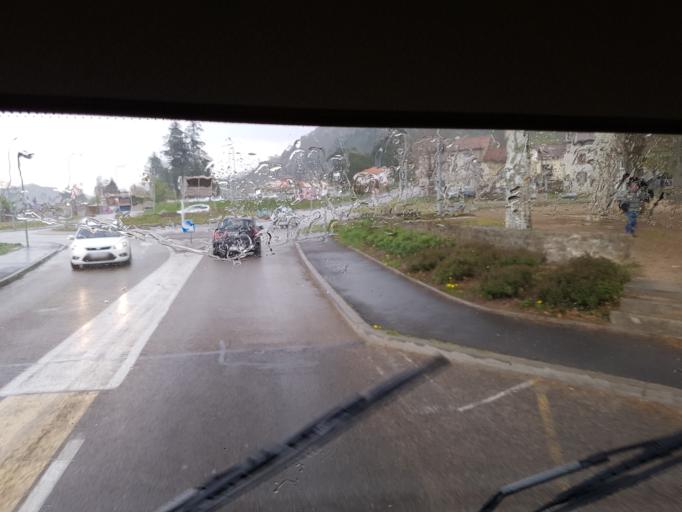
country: FR
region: Auvergne
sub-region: Departement de la Haute-Loire
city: Aurec-sur-Loire
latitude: 45.3706
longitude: 4.2064
